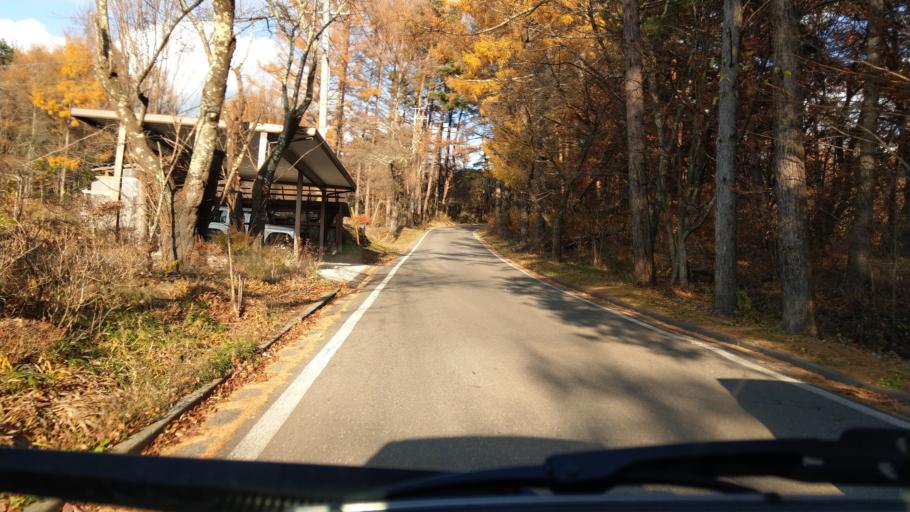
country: JP
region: Nagano
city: Komoro
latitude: 36.3468
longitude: 138.4545
